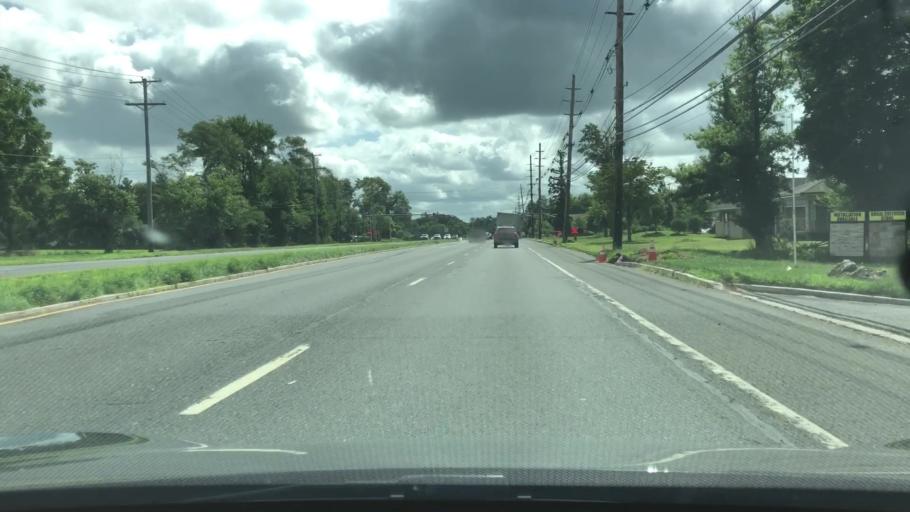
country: US
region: New Jersey
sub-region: Monmouth County
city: Englishtown
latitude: 40.2542
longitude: -74.3706
